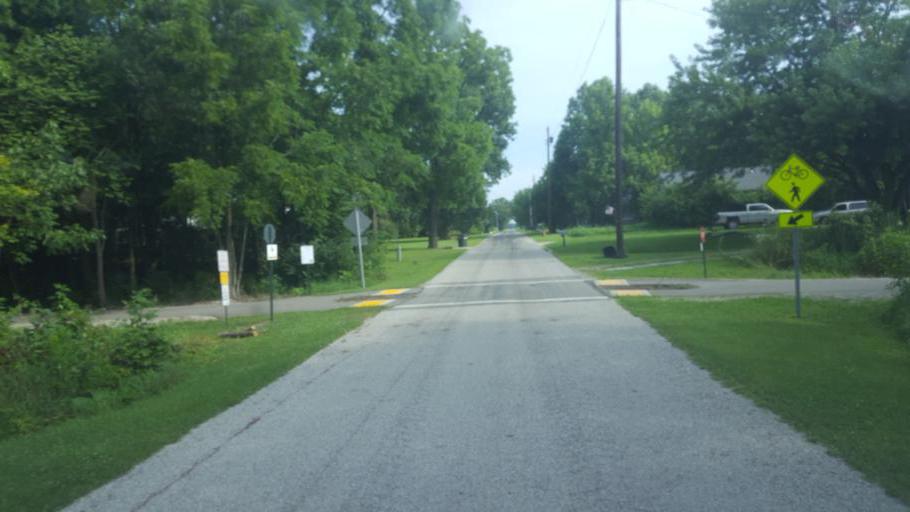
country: US
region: Ohio
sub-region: Marion County
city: Marion
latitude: 40.5978
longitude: -83.2554
